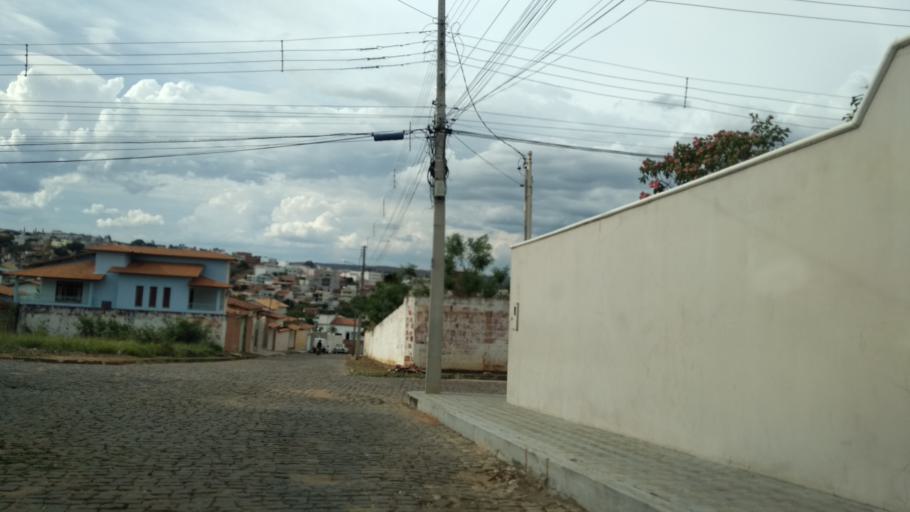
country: BR
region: Bahia
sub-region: Caetite
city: Caetite
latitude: -14.0711
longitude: -42.4798
